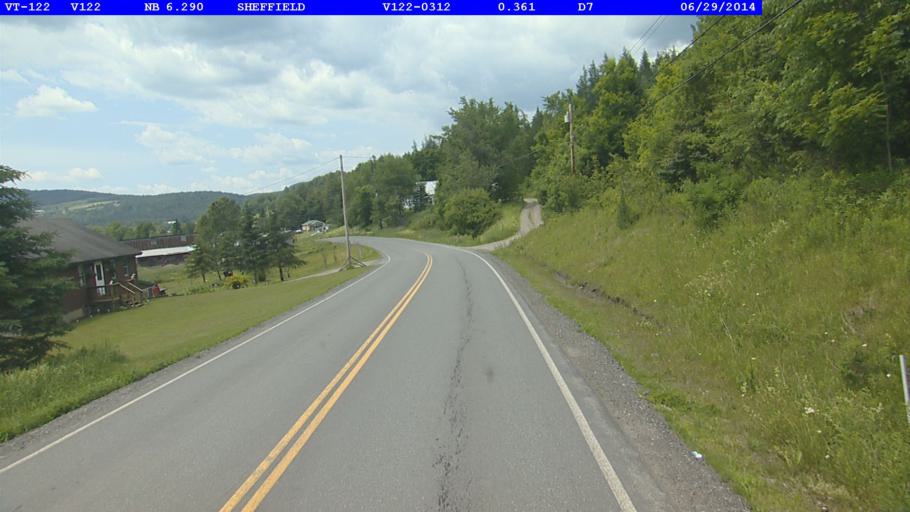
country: US
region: Vermont
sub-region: Caledonia County
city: Lyndonville
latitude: 44.5938
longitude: -72.0973
